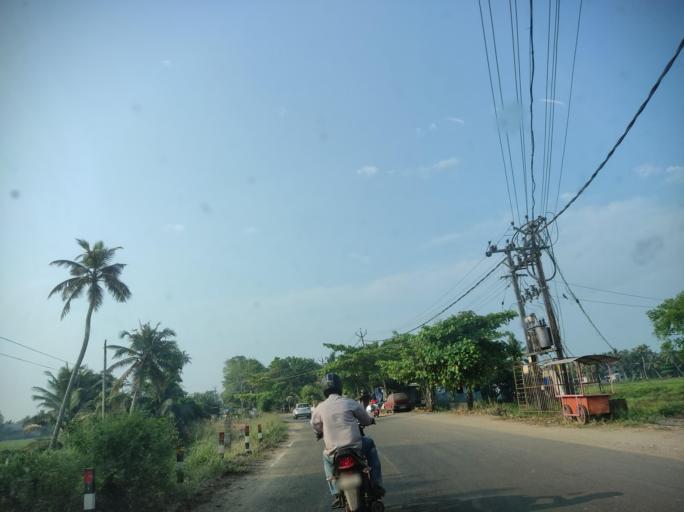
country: IN
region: Kerala
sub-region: Kottayam
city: Kottayam
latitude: 9.5767
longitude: 76.5004
